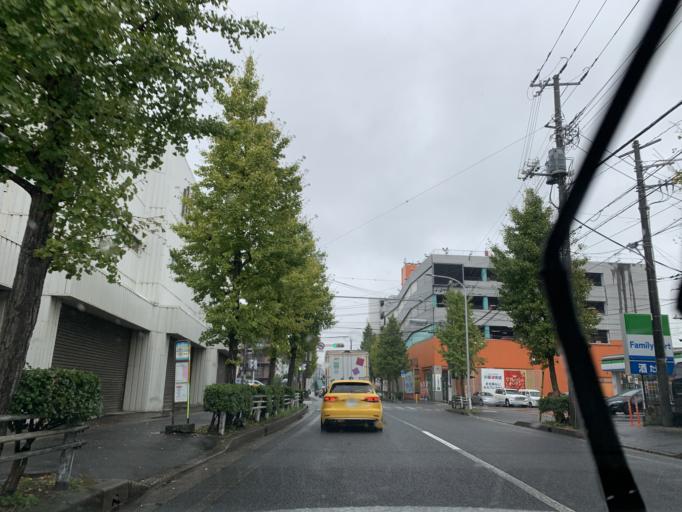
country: JP
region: Tokyo
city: Urayasu
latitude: 35.6646
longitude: 139.9024
